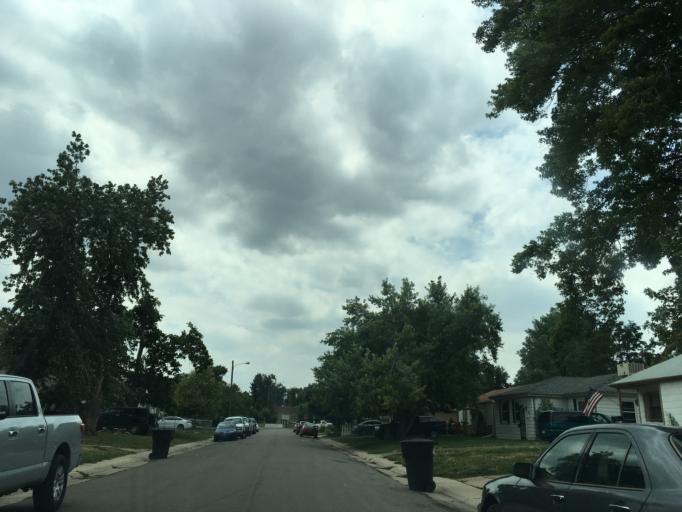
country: US
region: Colorado
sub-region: Arapahoe County
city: Sheridan
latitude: 39.6800
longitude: -105.0333
